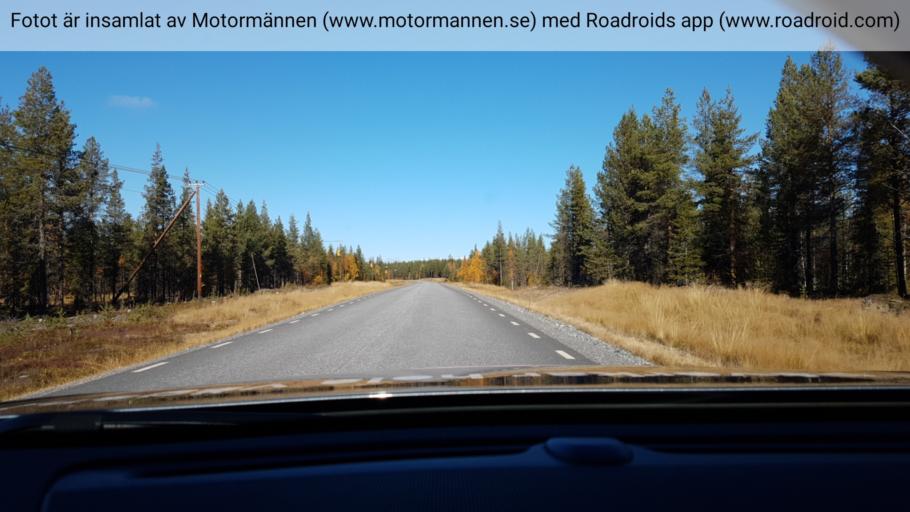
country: SE
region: Norrbotten
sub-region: Gallivare Kommun
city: Gaellivare
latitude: 66.8189
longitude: 21.0432
